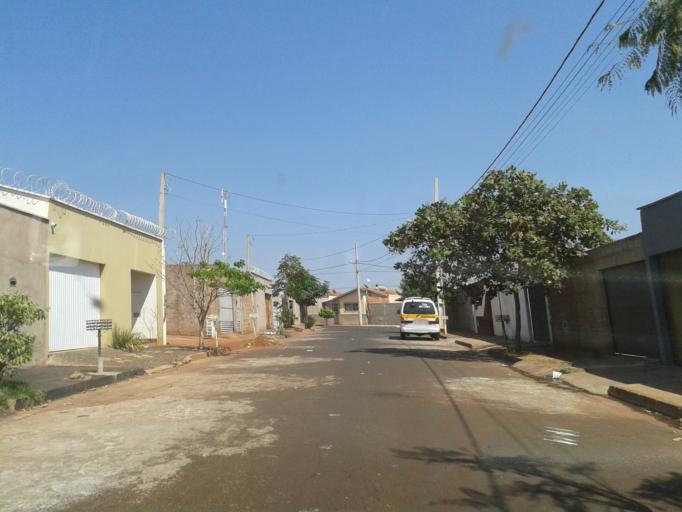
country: BR
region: Minas Gerais
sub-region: Ituiutaba
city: Ituiutaba
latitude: -19.0164
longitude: -49.4574
